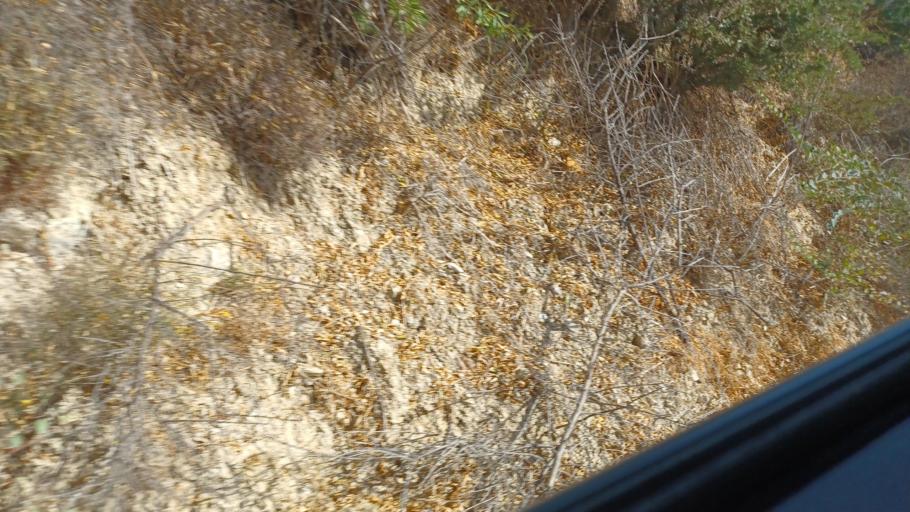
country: CY
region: Pafos
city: Tala
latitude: 34.8649
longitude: 32.4574
